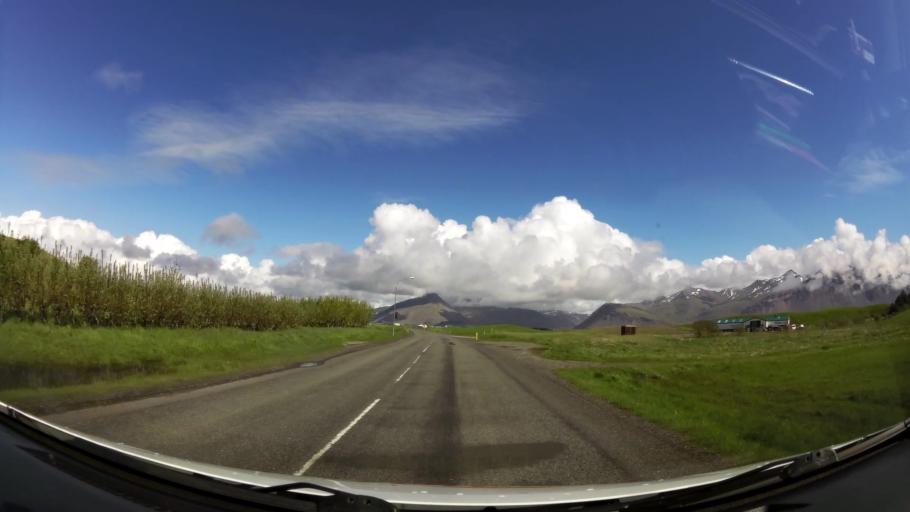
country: IS
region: East
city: Hoefn
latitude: 64.2671
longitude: -15.2017
